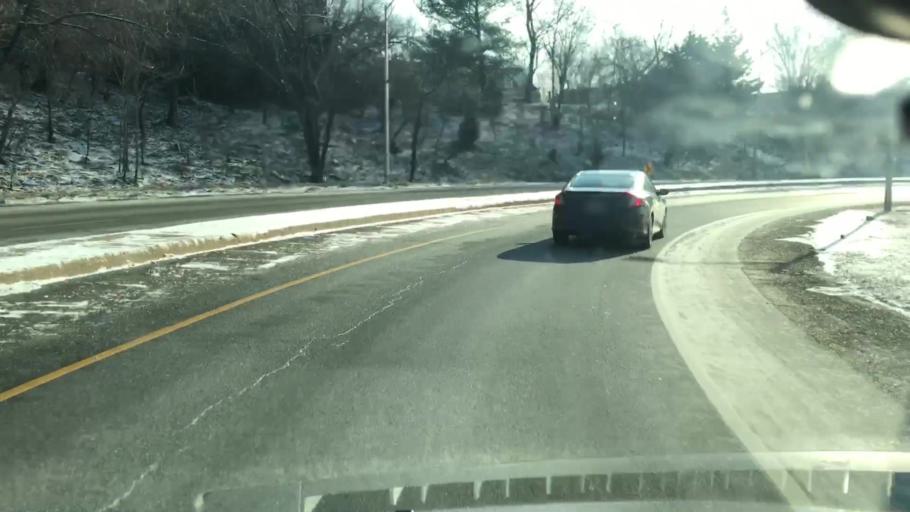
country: US
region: Virginia
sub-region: Fairfax County
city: Huntington
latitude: 38.8072
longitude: -77.0714
